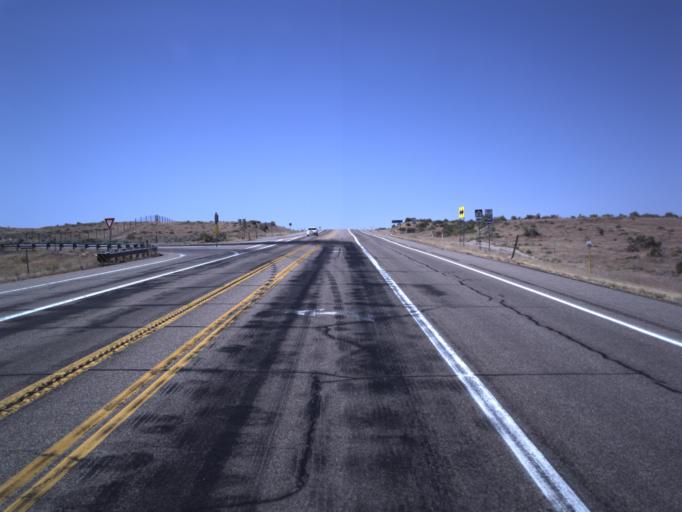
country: US
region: Utah
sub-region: Millard County
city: Delta
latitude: 39.3972
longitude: -112.5031
